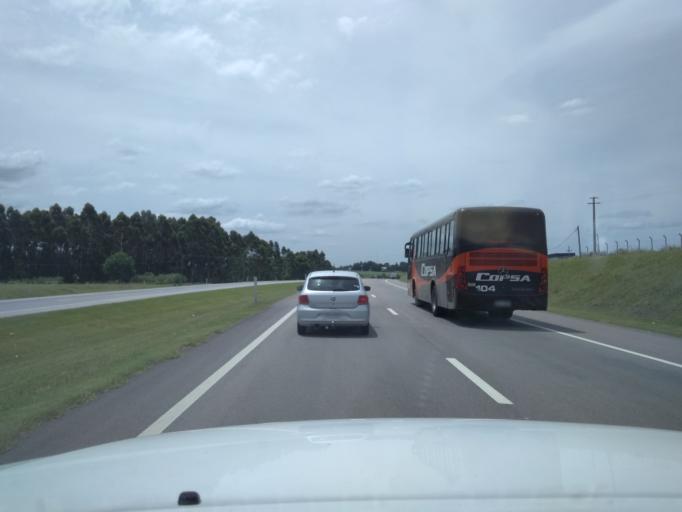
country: UY
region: Canelones
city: Progreso
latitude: -34.6848
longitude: -56.2405
